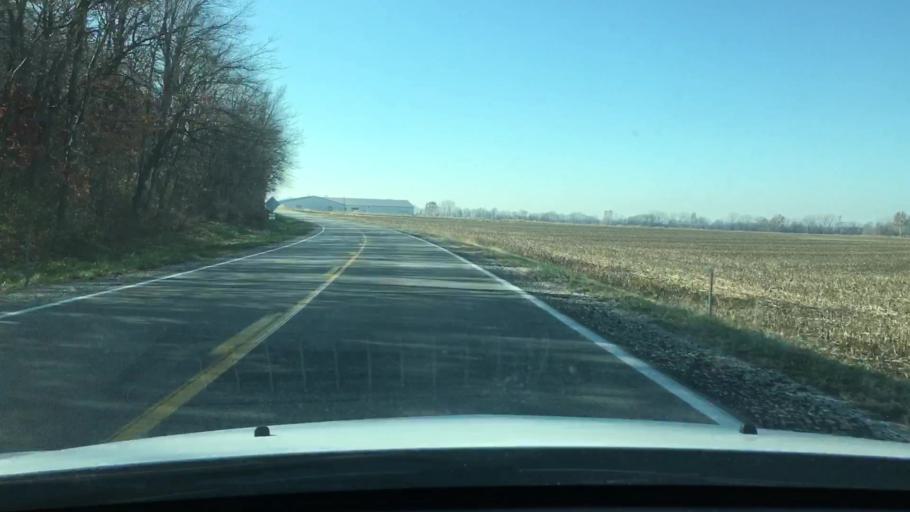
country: US
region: Illinois
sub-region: Morgan County
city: Meredosia
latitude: 39.7351
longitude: -90.5611
